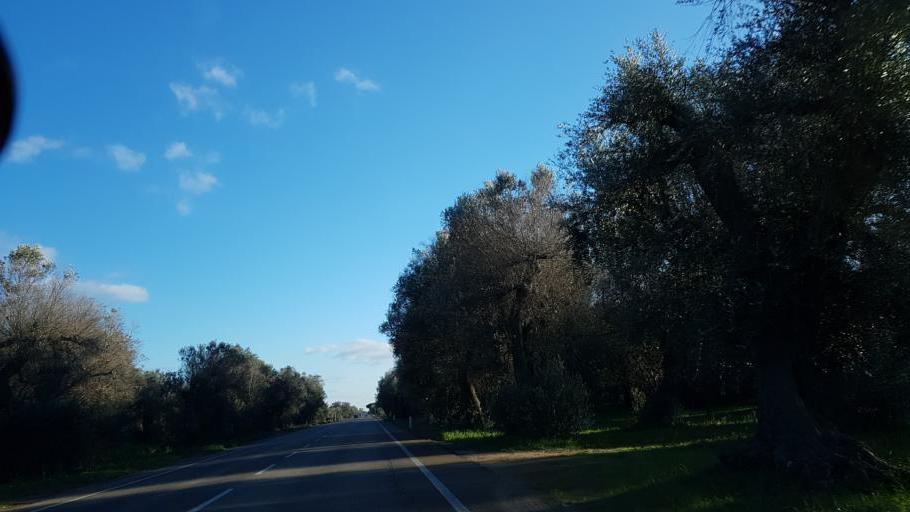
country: IT
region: Apulia
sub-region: Provincia di Lecce
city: Squinzano
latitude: 40.4588
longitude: 18.0221
